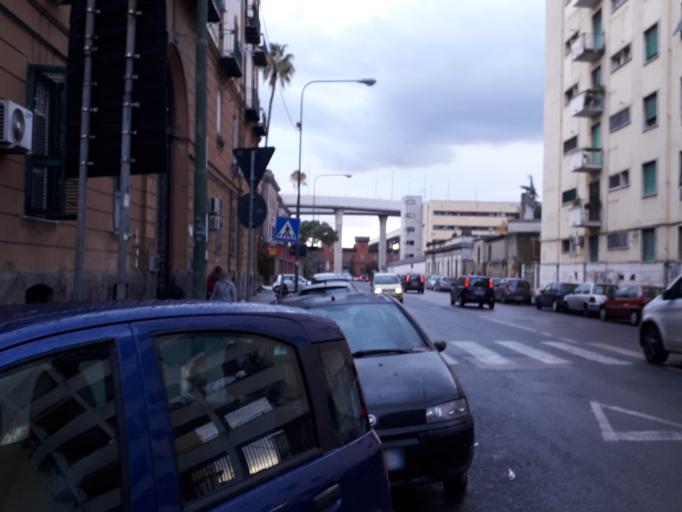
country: IT
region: Campania
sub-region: Provincia di Napoli
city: Napoli
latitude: 40.8633
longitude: 14.2729
